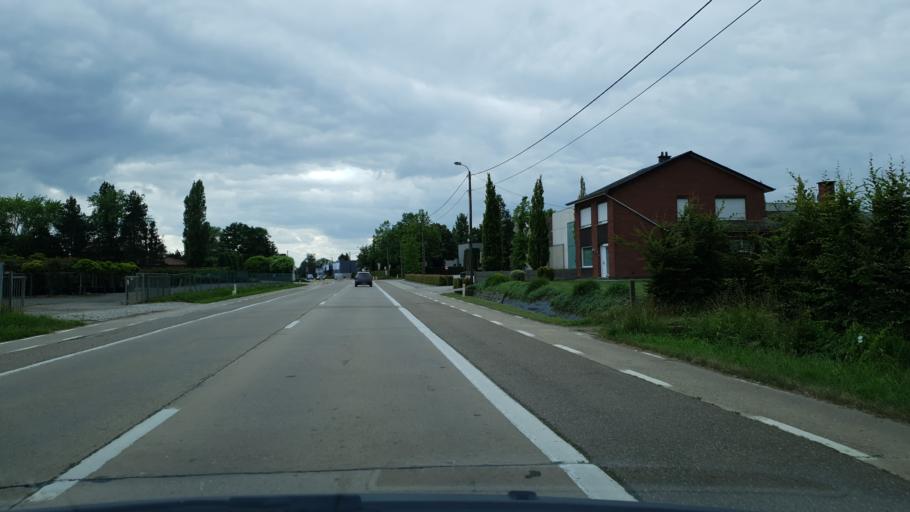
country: BE
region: Flanders
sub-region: Provincie Antwerpen
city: Hulshout
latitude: 51.0589
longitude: 4.8145
